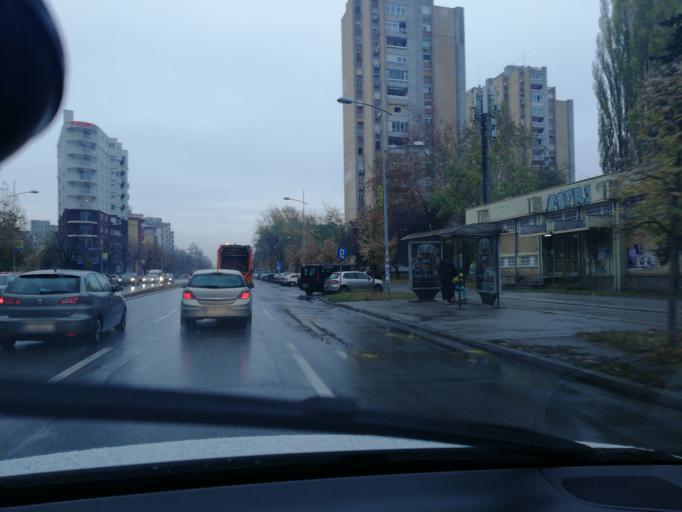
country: RS
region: Autonomna Pokrajina Vojvodina
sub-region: Juznobacki Okrug
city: Novi Sad
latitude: 45.2414
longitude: 19.8315
